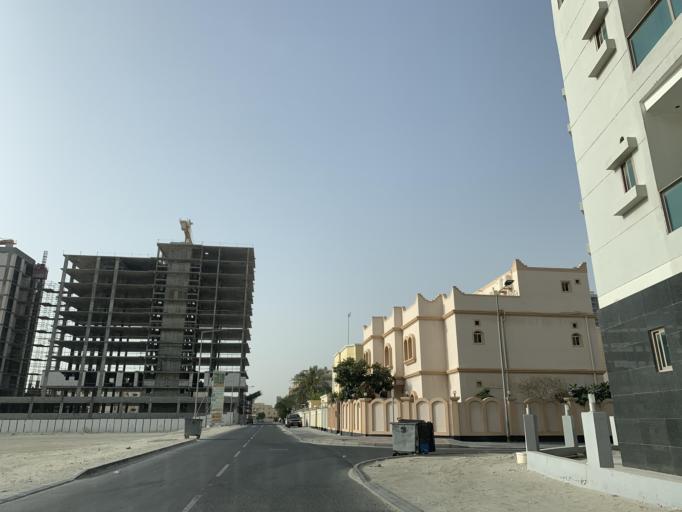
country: BH
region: Manama
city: Manama
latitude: 26.2188
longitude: 50.6141
